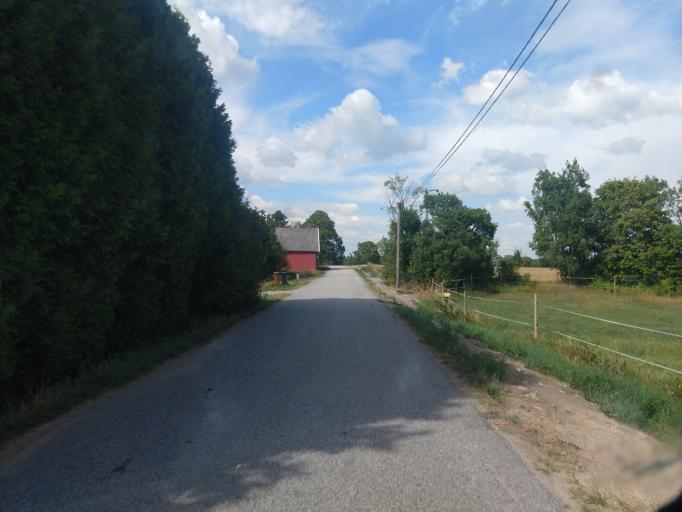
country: SE
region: Blekinge
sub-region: Karlskrona Kommun
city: Nattraby
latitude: 56.2503
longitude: 15.5266
